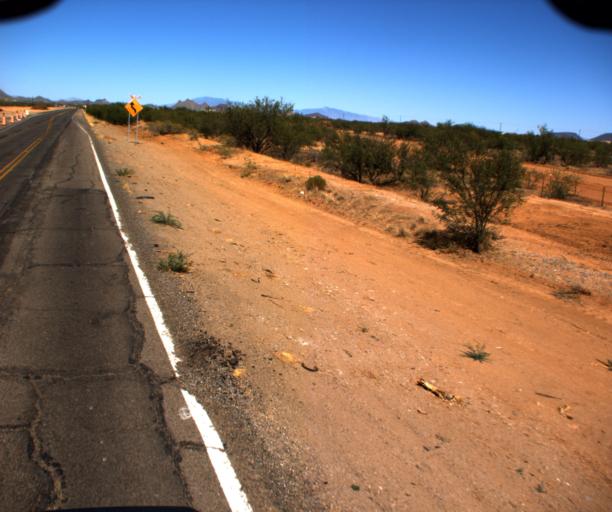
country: US
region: Arizona
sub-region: Pima County
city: Valencia West
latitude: 32.1387
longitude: -111.1565
